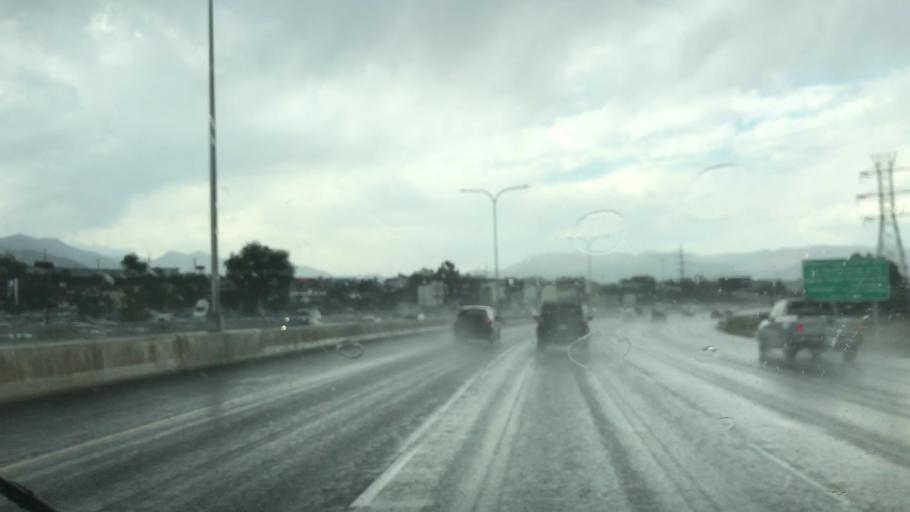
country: US
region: Colorado
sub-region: El Paso County
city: Colorado Springs
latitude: 38.8197
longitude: -104.8345
